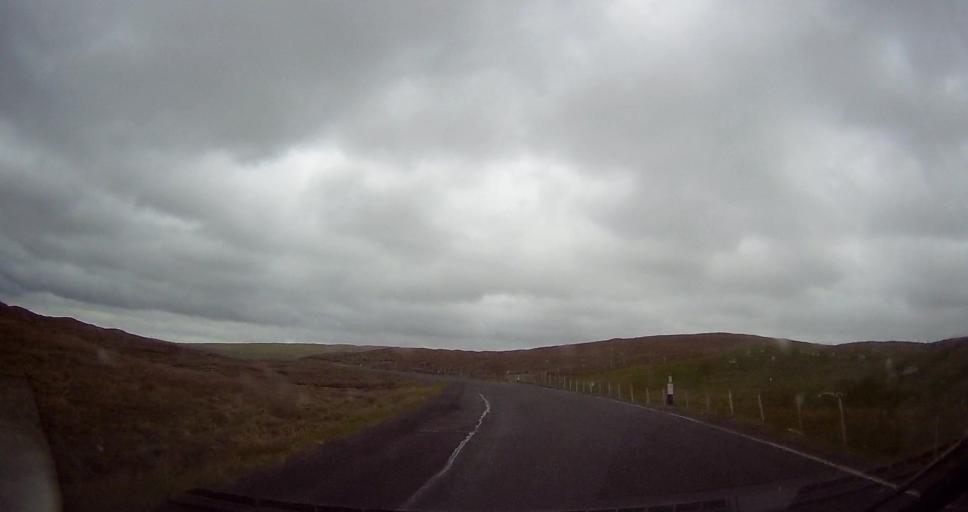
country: GB
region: Scotland
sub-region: Shetland Islands
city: Lerwick
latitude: 60.4803
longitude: -1.4197
